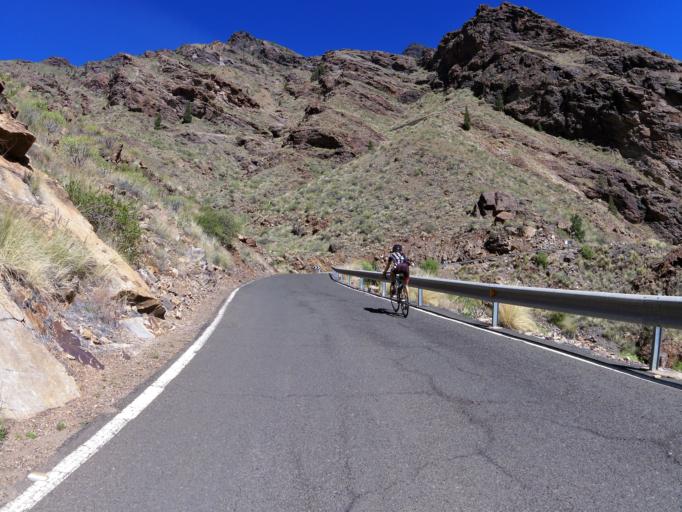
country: ES
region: Canary Islands
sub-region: Provincia de Las Palmas
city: Artenara
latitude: 27.9918
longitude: -15.7101
